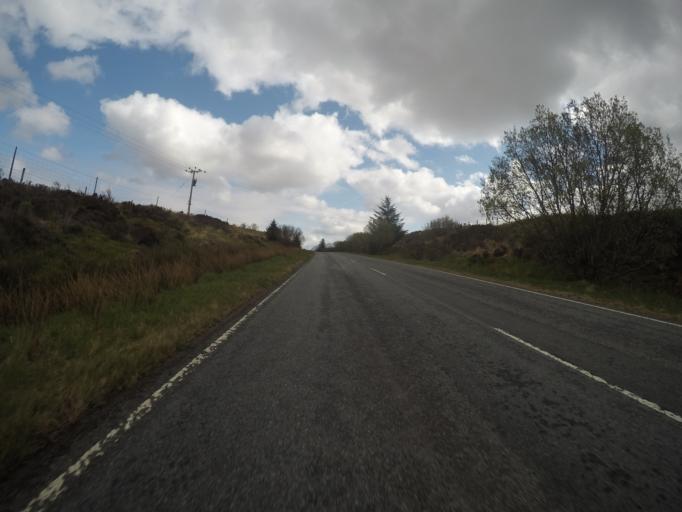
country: GB
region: Scotland
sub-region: Highland
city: Isle of Skye
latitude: 57.3339
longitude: -6.3493
